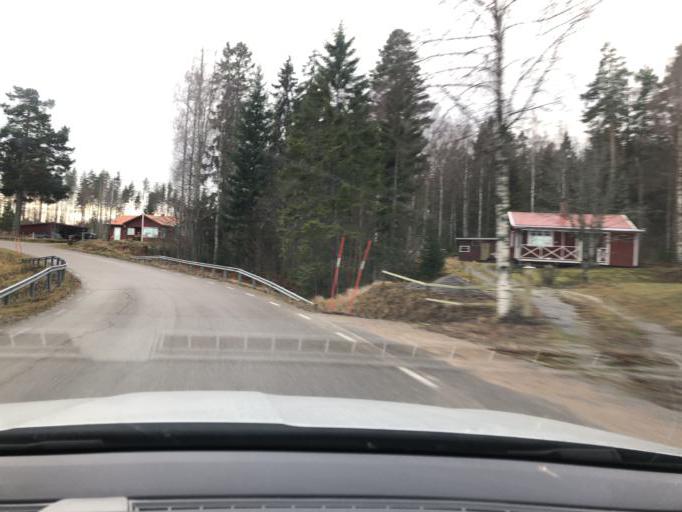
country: SE
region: Gaevleborg
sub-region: Hudiksvalls Kommun
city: Sorforsa
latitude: 61.6580
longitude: 16.9252
